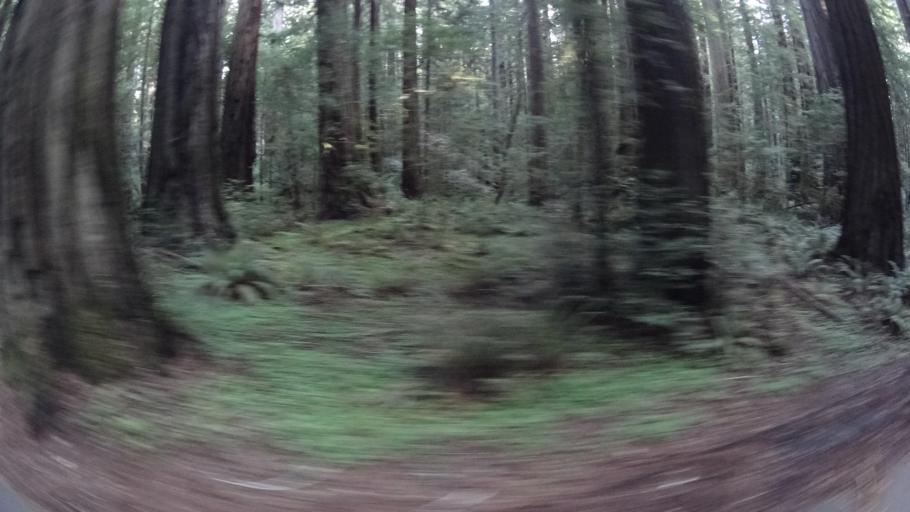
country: US
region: California
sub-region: Humboldt County
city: Rio Dell
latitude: 40.3513
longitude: -124.0017
